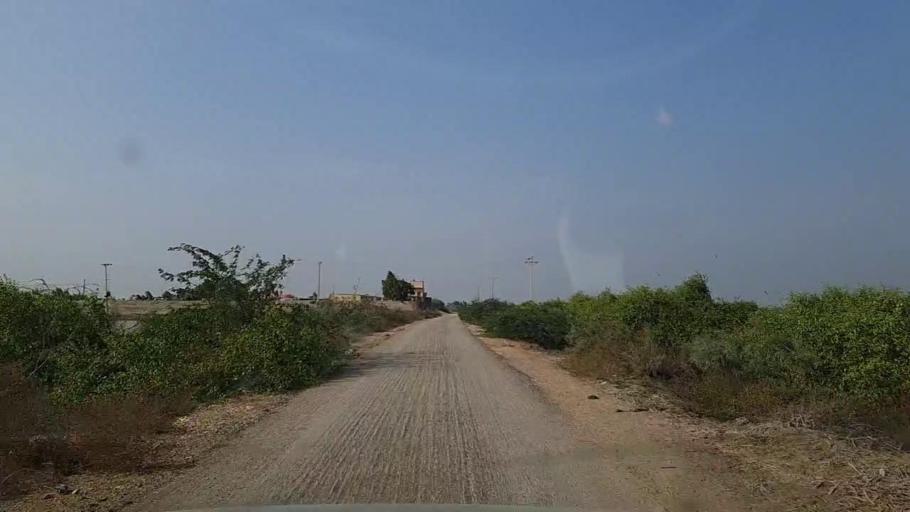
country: PK
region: Sindh
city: Mirpur Sakro
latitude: 24.5741
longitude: 67.5712
